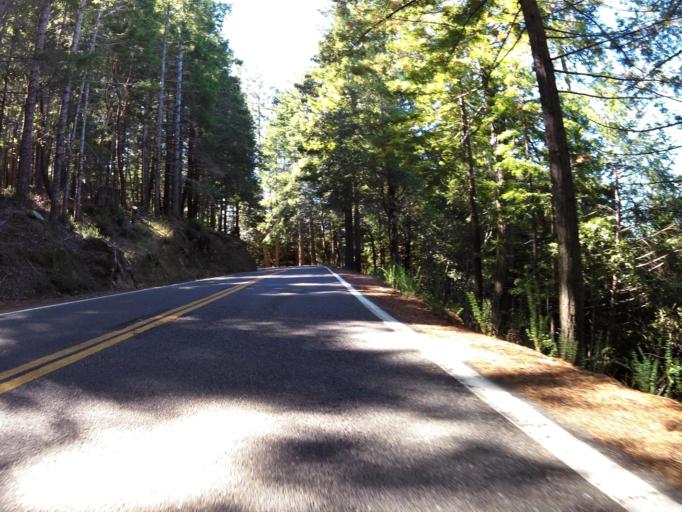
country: US
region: California
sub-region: Humboldt County
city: Redway
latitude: 39.8271
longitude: -123.7784
